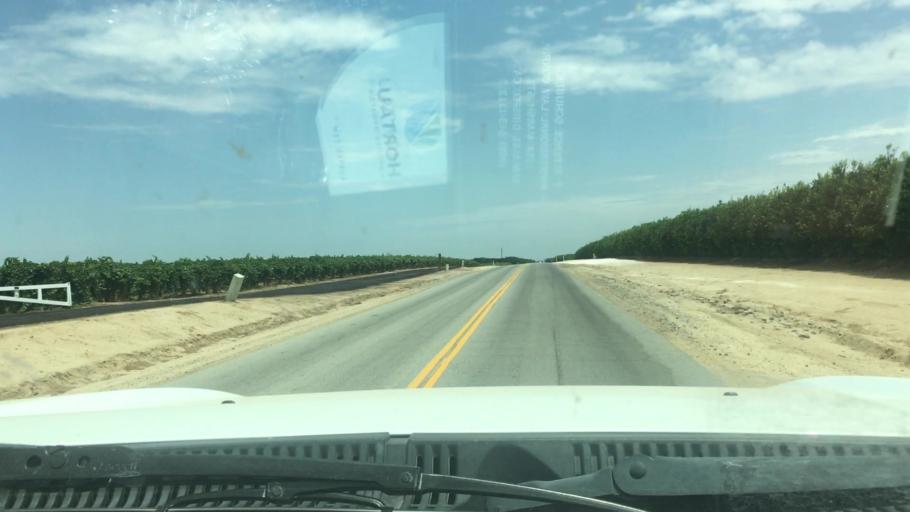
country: US
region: California
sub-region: Kern County
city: McFarland
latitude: 35.5679
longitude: -119.1511
